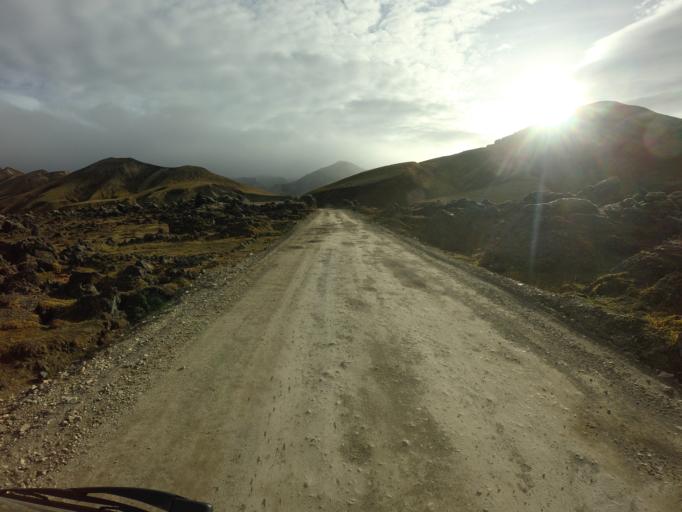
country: IS
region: South
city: Vestmannaeyjar
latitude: 64.0000
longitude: -19.0508
